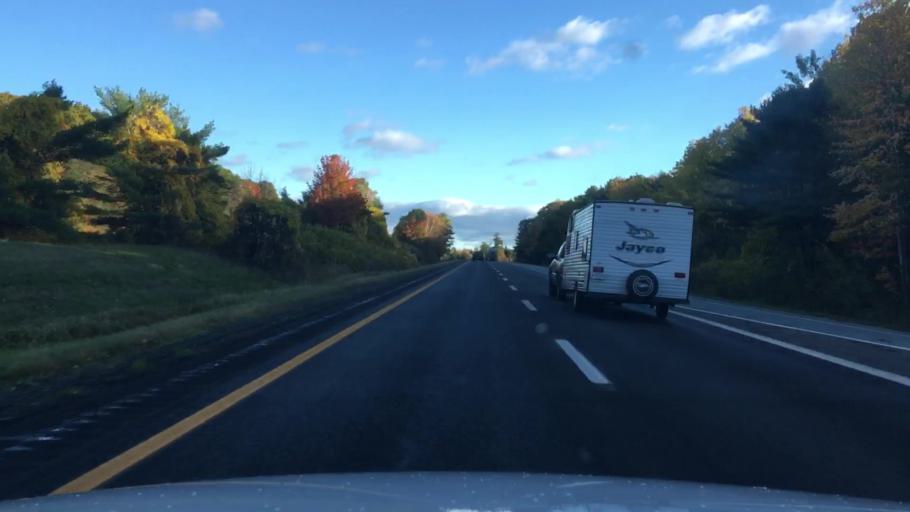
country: US
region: Maine
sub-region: Penobscot County
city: Orono
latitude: 44.8746
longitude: -68.7010
